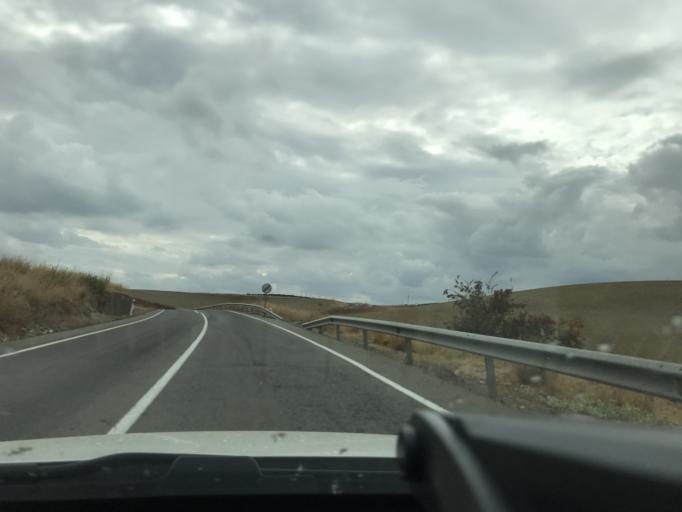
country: ES
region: Andalusia
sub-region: Provincia de Sevilla
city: Cantillana
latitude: 37.6186
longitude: -5.7933
